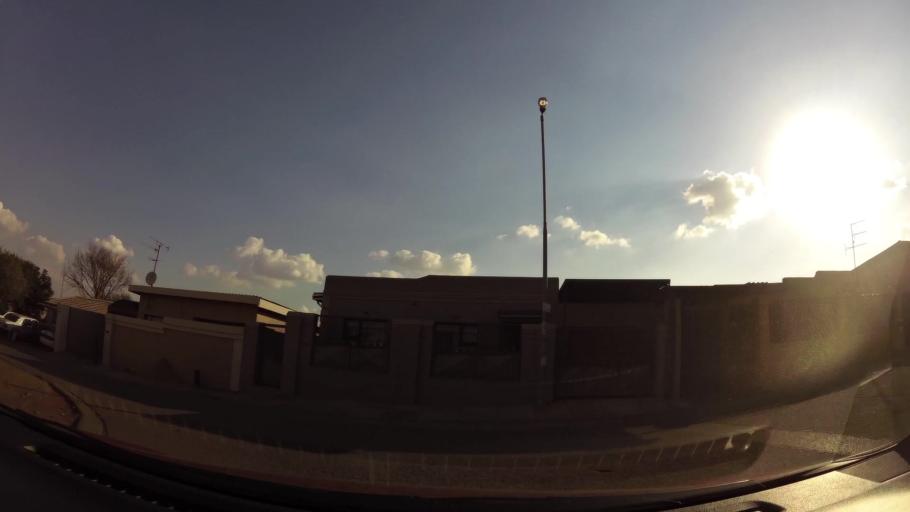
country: ZA
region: Gauteng
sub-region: City of Johannesburg Metropolitan Municipality
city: Soweto
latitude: -26.2335
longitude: 27.8605
